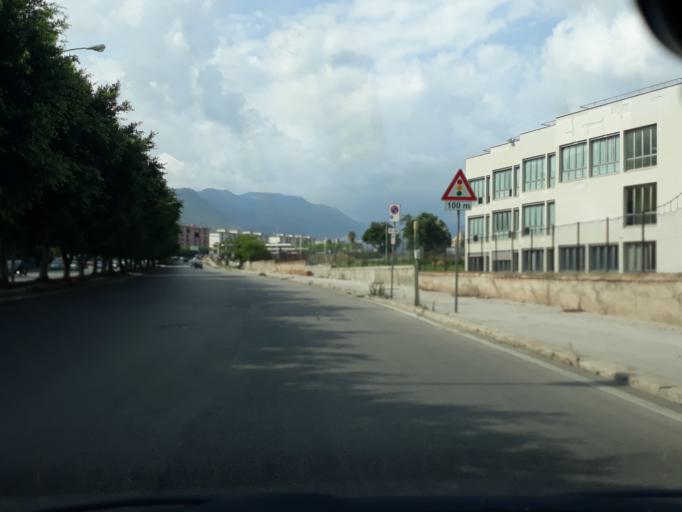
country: IT
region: Sicily
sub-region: Palermo
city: Palermo
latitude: 38.1021
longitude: 13.3481
